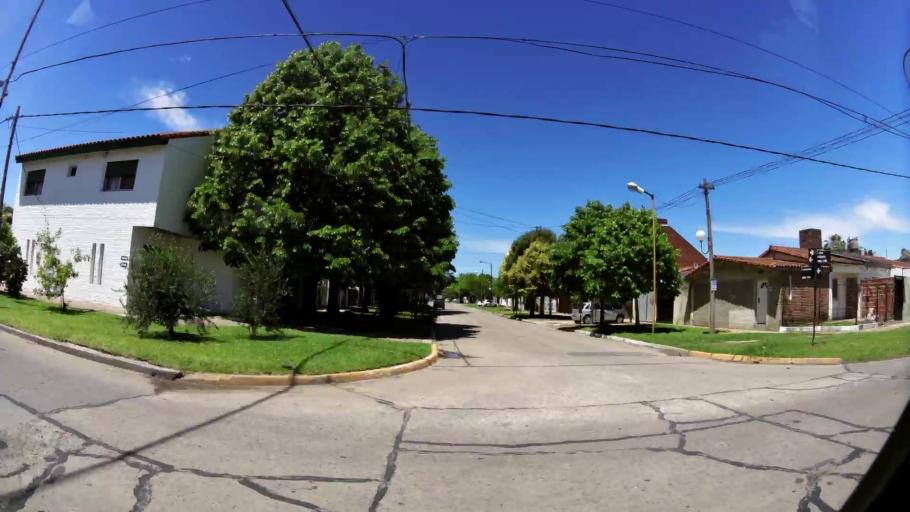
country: AR
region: Buenos Aires
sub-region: Partido de Quilmes
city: Quilmes
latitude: -34.7317
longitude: -58.2771
